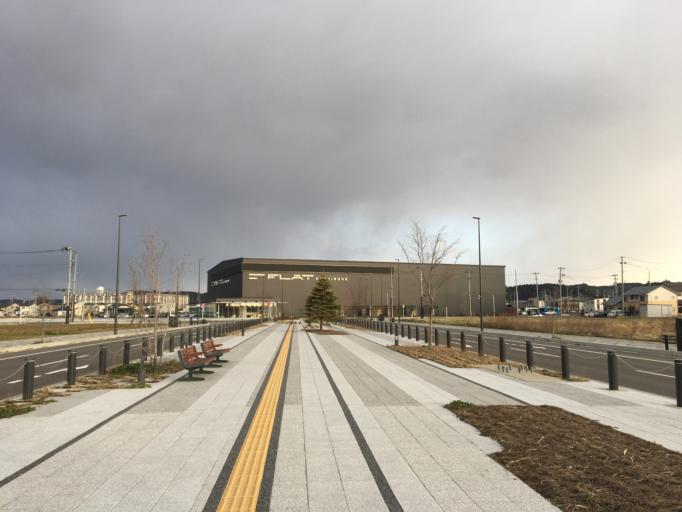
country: JP
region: Aomori
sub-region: Hachinohe Shi
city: Uchimaru
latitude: 40.5104
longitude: 141.4298
